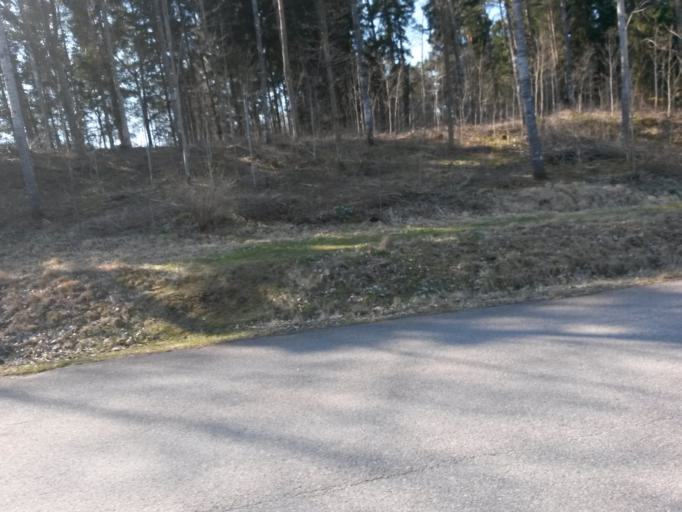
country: SE
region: Vaestra Goetaland
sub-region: Vargarda Kommun
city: Vargarda
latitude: 58.0250
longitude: 12.7974
